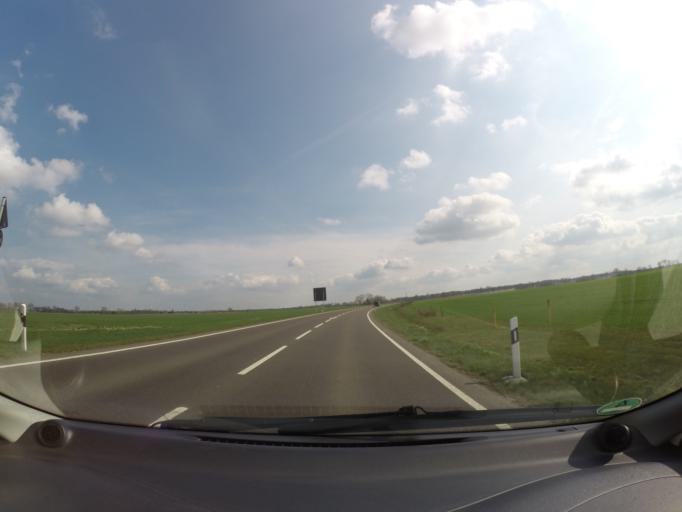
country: DE
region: Brandenburg
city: Rehfelde
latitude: 52.4884
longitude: 13.8734
